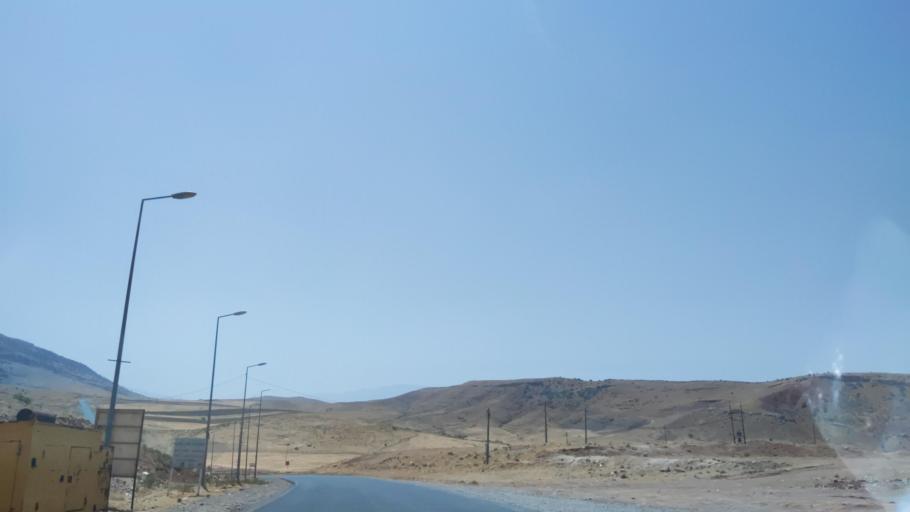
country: IQ
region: Arbil
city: Shaqlawah
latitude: 36.6078
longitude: 44.3091
